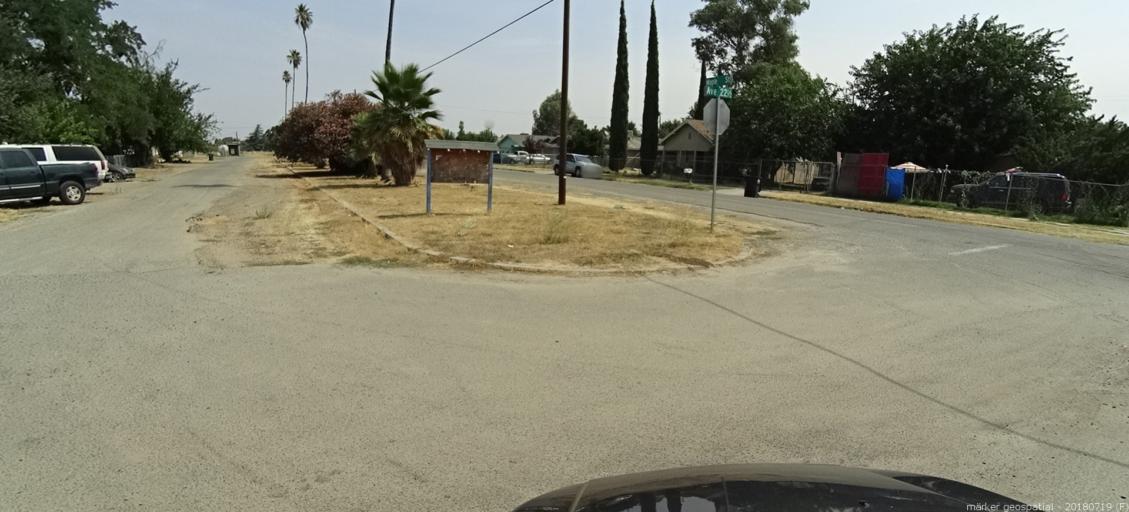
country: US
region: California
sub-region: Madera County
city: Fairmead
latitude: 37.0764
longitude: -120.1959
